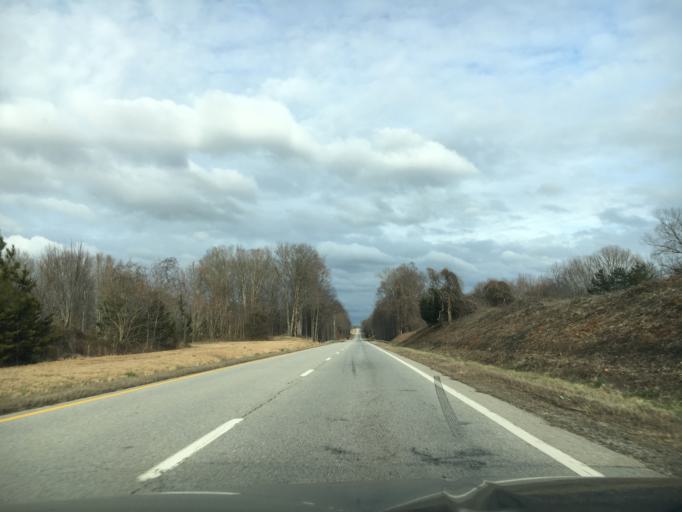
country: US
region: Virginia
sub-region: Lunenburg County
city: Victoria
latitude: 37.1433
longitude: -78.2999
